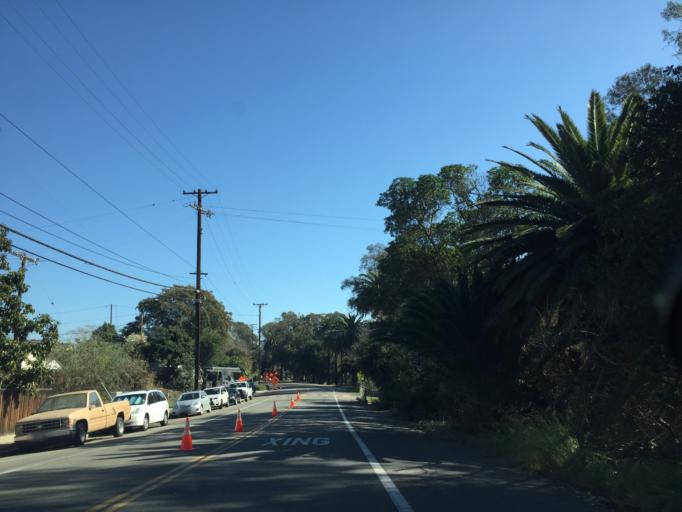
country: US
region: California
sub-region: Santa Barbara County
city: Mission Canyon
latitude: 34.4385
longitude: -119.7673
